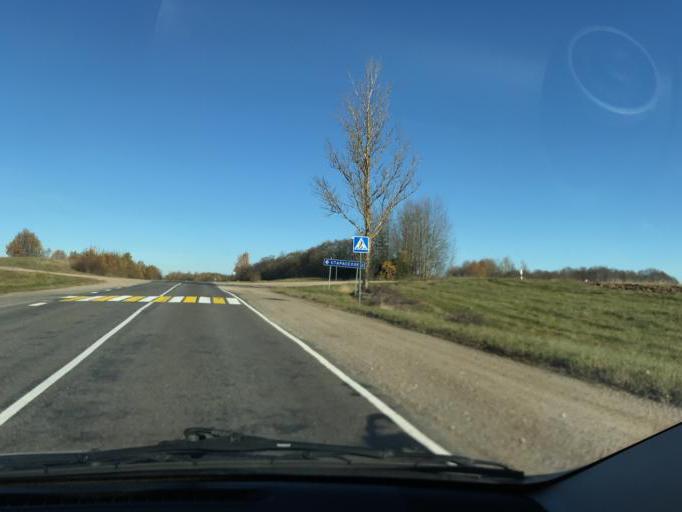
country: BY
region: Vitebsk
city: Lyepyel'
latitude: 55.0301
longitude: 28.7465
